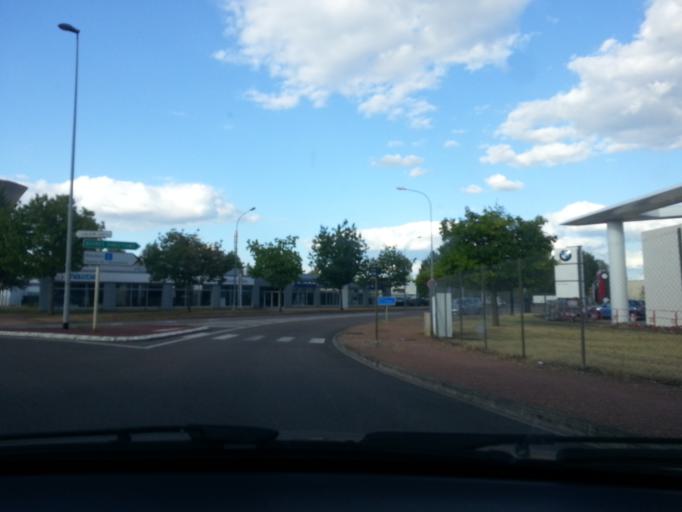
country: FR
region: Bourgogne
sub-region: Departement de Saone-et-Loire
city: Chalon-sur-Saone
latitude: 46.7688
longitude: 4.8594
